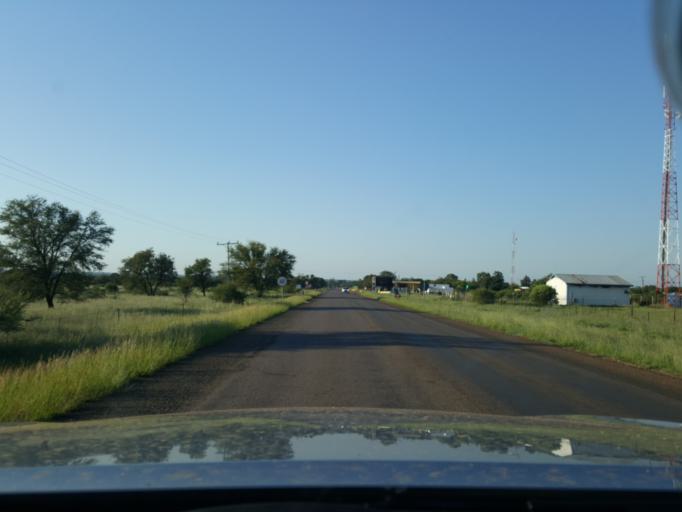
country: BW
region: South East
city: Janeng
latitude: -25.6286
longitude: 25.5744
